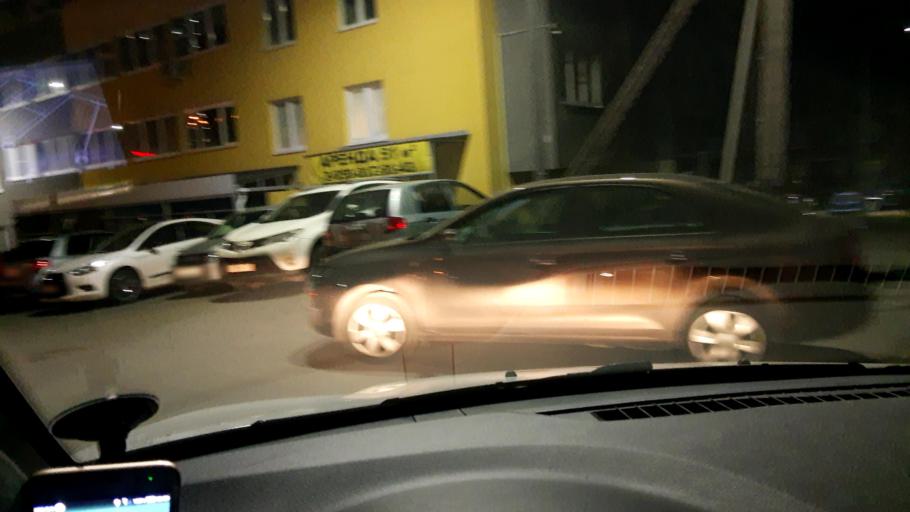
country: RU
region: Nizjnij Novgorod
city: Afonino
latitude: 56.2761
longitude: 44.0863
